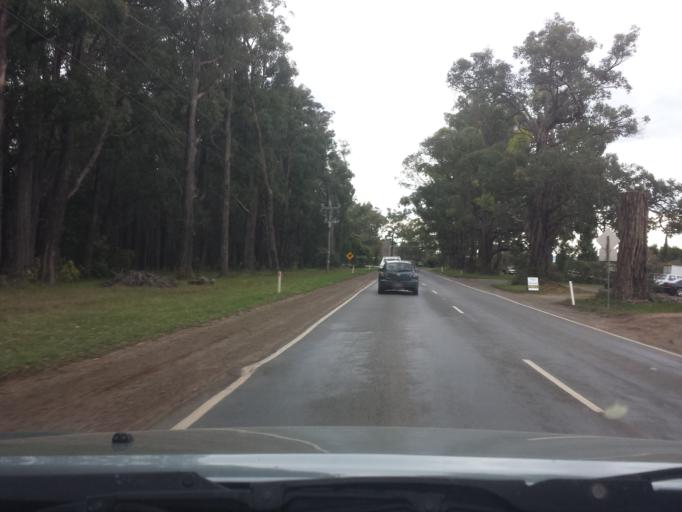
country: AU
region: Victoria
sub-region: Yarra Ranges
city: Kalorama
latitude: -37.8220
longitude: 145.4133
